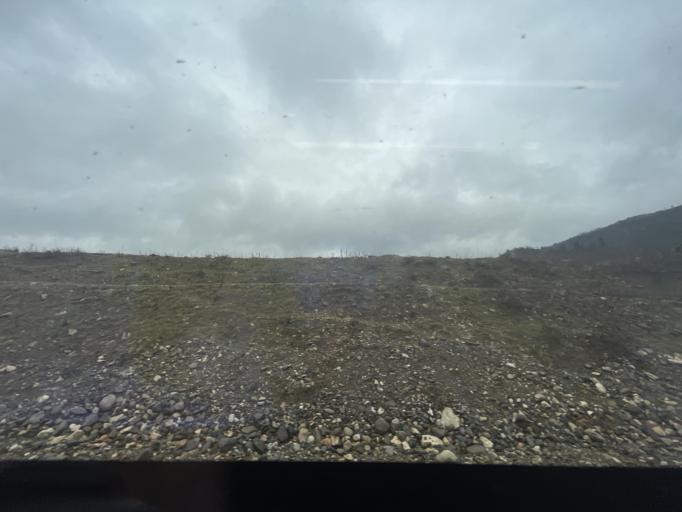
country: GE
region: Imereti
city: Kharagauli
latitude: 42.0231
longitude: 43.2025
